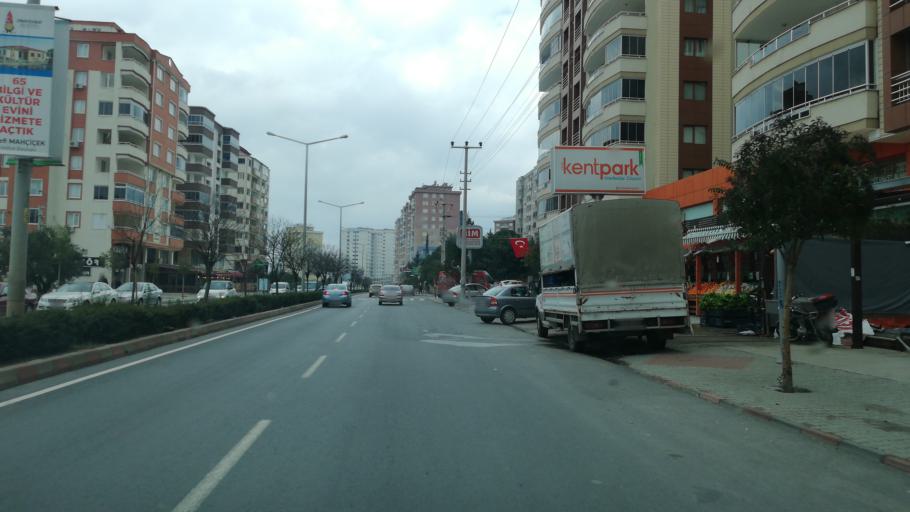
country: TR
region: Kahramanmaras
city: Kahramanmaras
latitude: 37.5842
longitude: 36.8663
